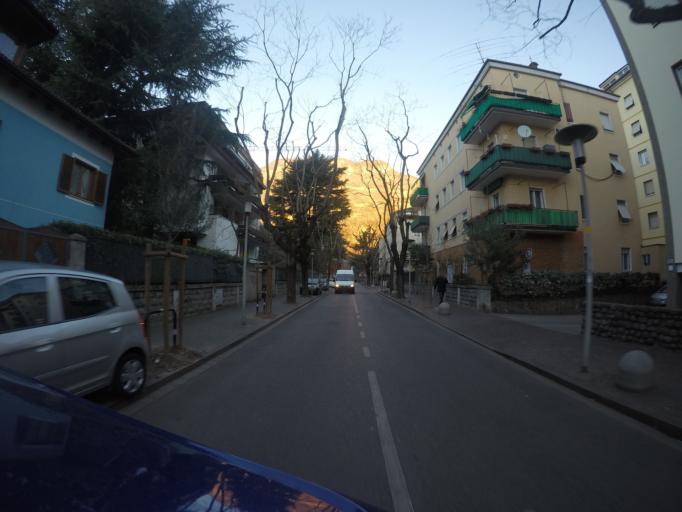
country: IT
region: Trentino-Alto Adige
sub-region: Bolzano
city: Bolzano
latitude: 46.5038
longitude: 11.3416
